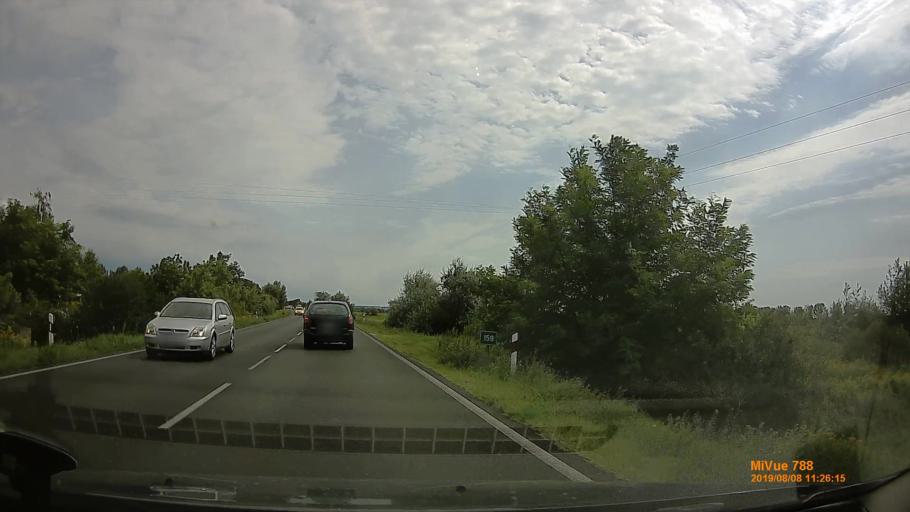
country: HU
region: Somogy
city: Balatonfenyves
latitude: 46.7000
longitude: 17.4389
